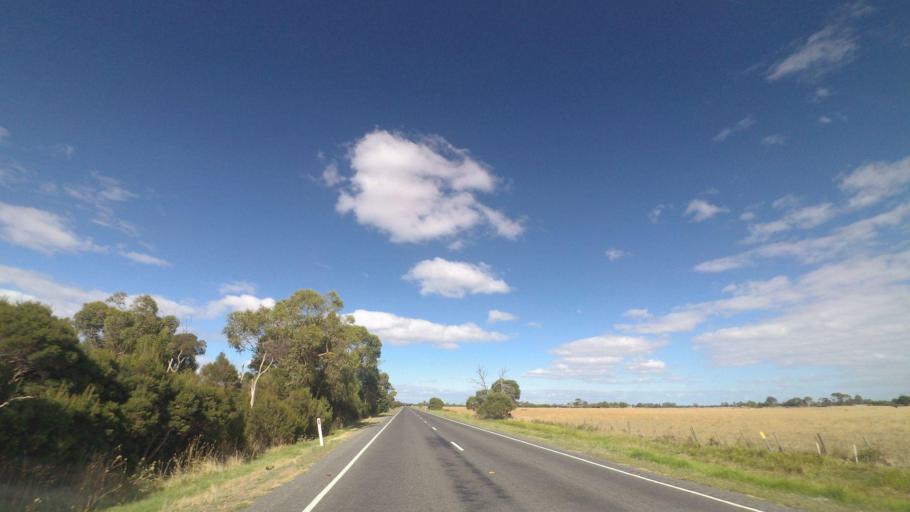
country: AU
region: Victoria
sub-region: Cardinia
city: Pakenham South
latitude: -38.1828
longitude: 145.5531
